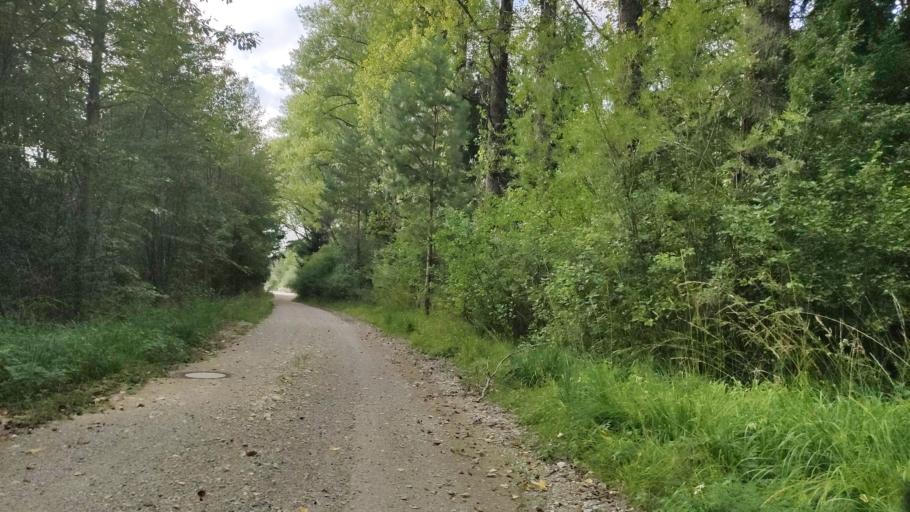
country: DE
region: Bavaria
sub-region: Upper Bavaria
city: Prittriching
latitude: 48.2150
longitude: 10.8968
